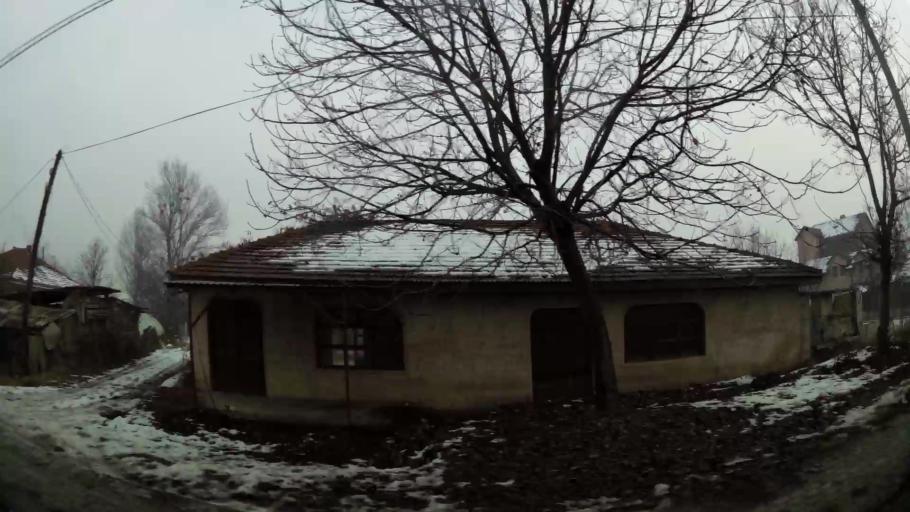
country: MK
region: Ilinden
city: Idrizovo
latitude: 41.9548
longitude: 21.5762
